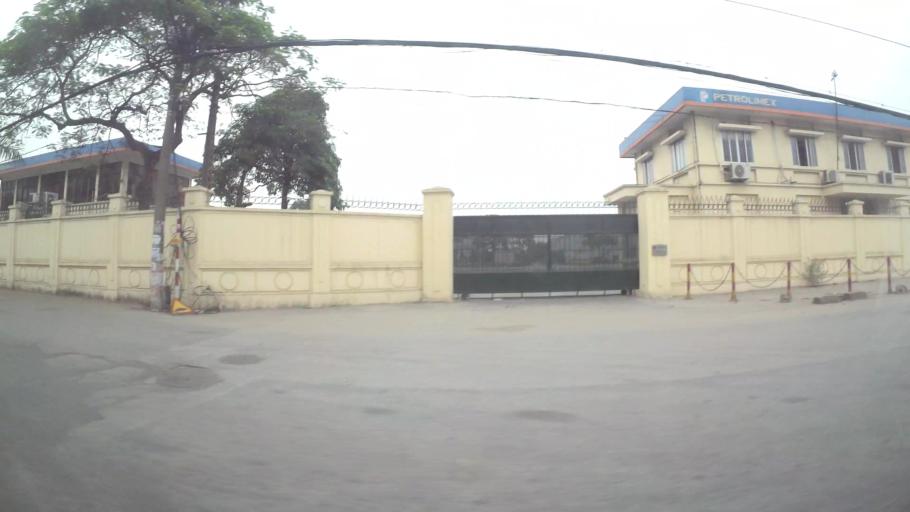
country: VN
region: Ha Noi
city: Hoan Kiem
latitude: 21.0666
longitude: 105.8917
